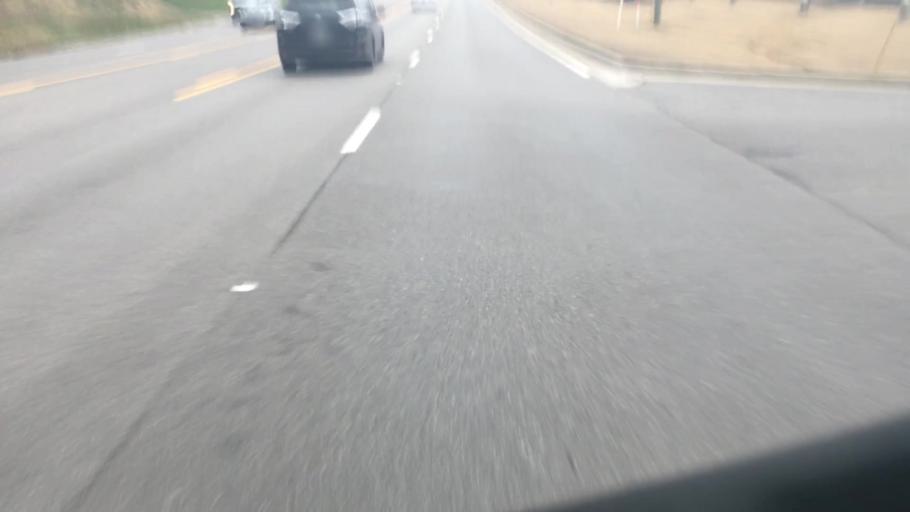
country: US
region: Alabama
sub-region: Jefferson County
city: Hoover
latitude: 33.3594
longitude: -86.8327
